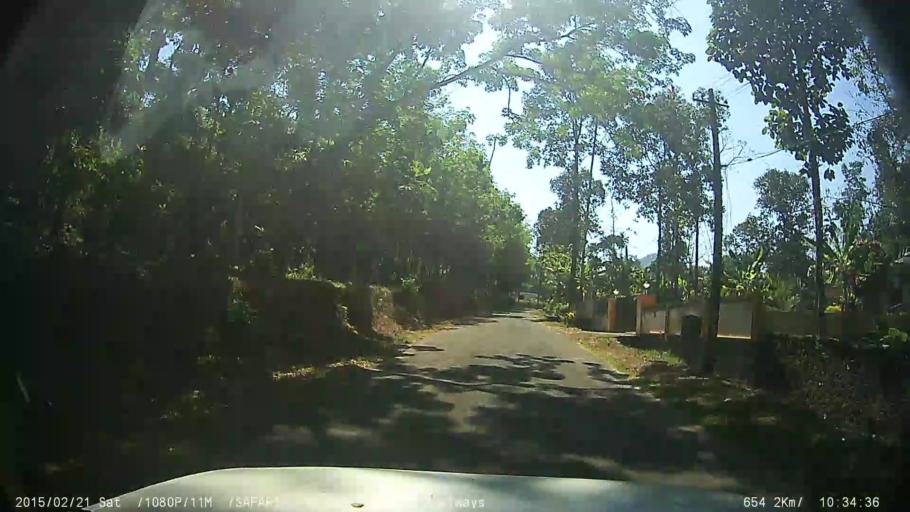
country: IN
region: Kerala
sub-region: Kottayam
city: Lalam
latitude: 9.8272
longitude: 76.7192
